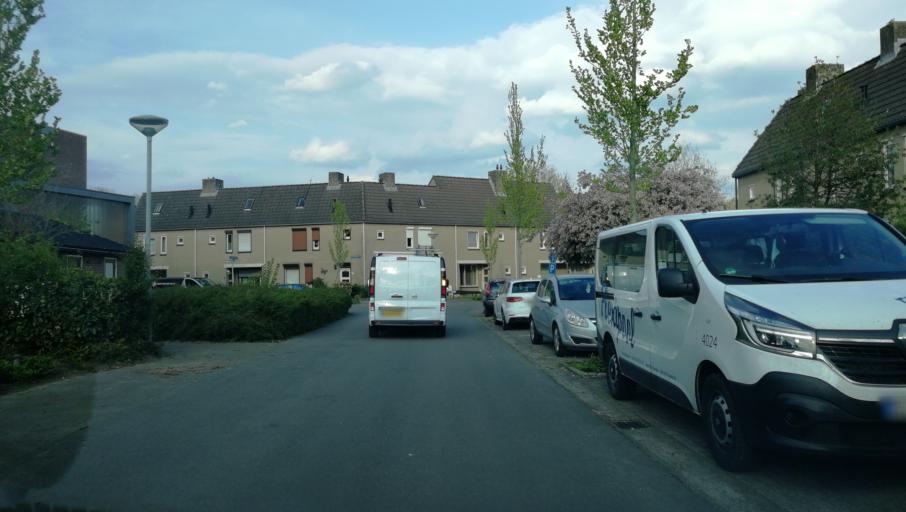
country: NL
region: Limburg
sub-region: Gemeente Venlo
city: Tegelen
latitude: 51.3767
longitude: 6.1302
